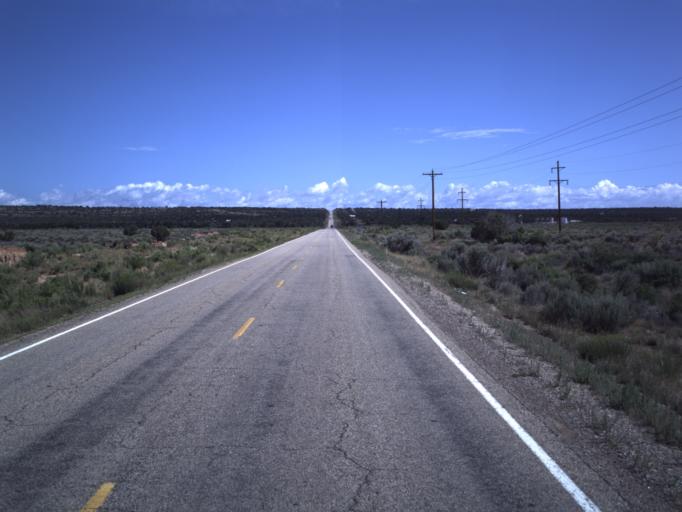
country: US
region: Utah
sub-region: Duchesne County
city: Duchesne
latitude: 40.2756
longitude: -110.3797
